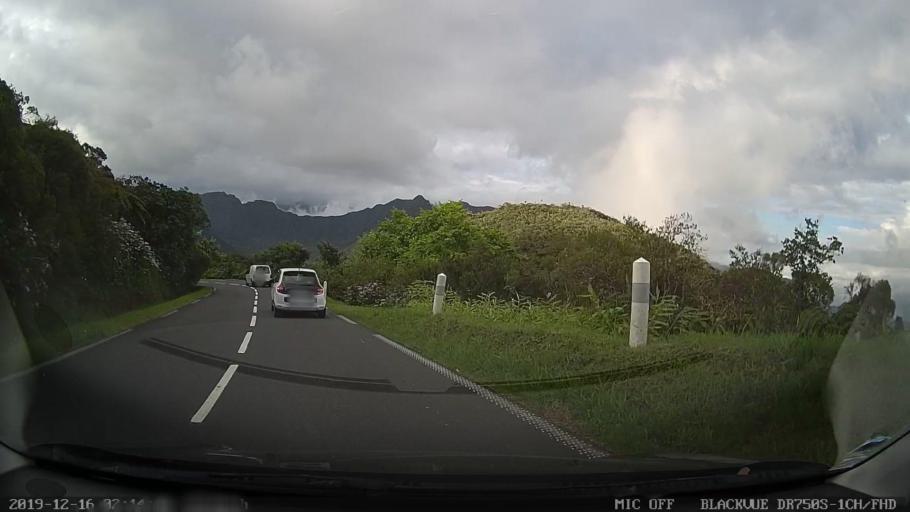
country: RE
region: Reunion
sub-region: Reunion
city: Cilaos
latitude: -21.1604
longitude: 55.5980
